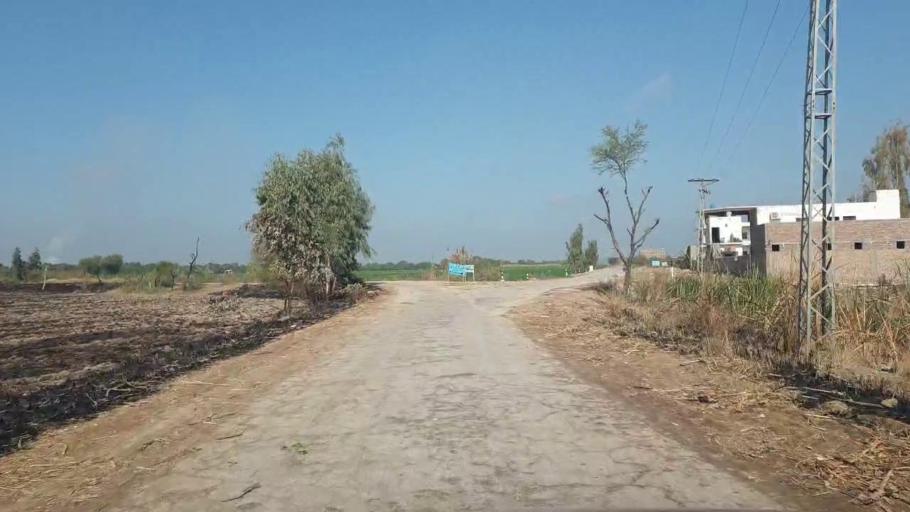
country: PK
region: Sindh
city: Shahdadpur
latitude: 25.9108
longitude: 68.5955
